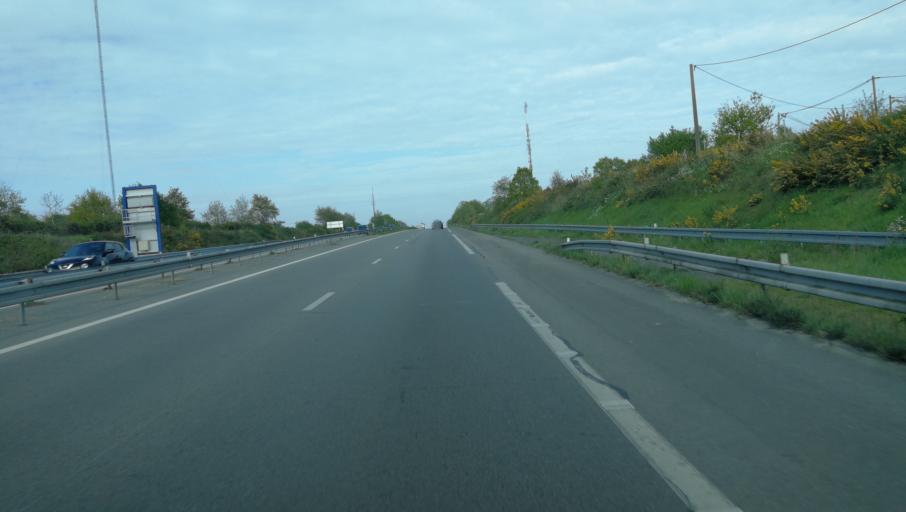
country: FR
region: Pays de la Loire
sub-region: Departement de la Loire-Atlantique
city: Thouare-sur-Loire
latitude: 47.2996
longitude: -1.4347
